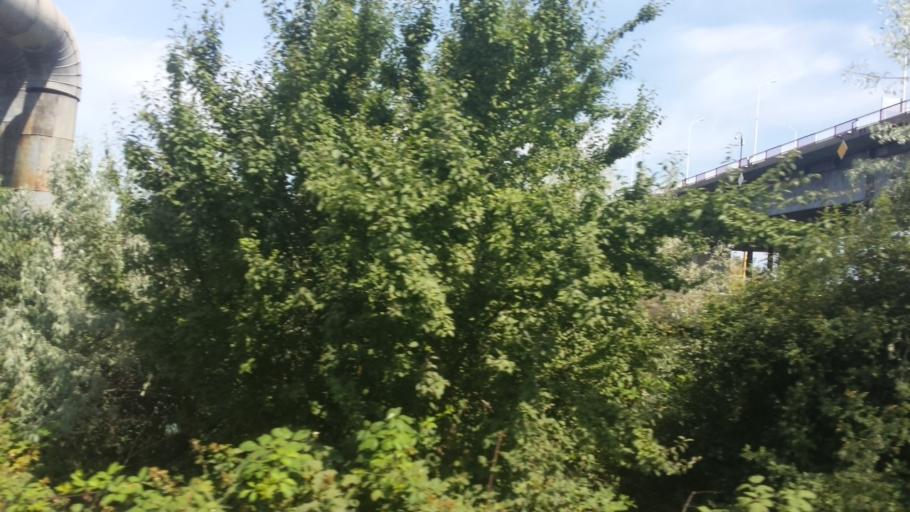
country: RO
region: Constanta
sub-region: Comuna Navodari
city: Navodari
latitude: 44.3232
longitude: 28.6195
